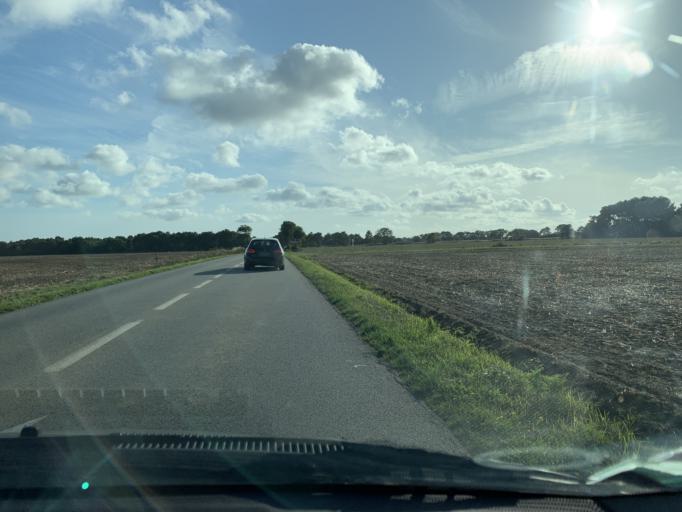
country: FR
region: Brittany
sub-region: Departement du Morbihan
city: Sarzeau
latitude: 47.5536
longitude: -2.7064
